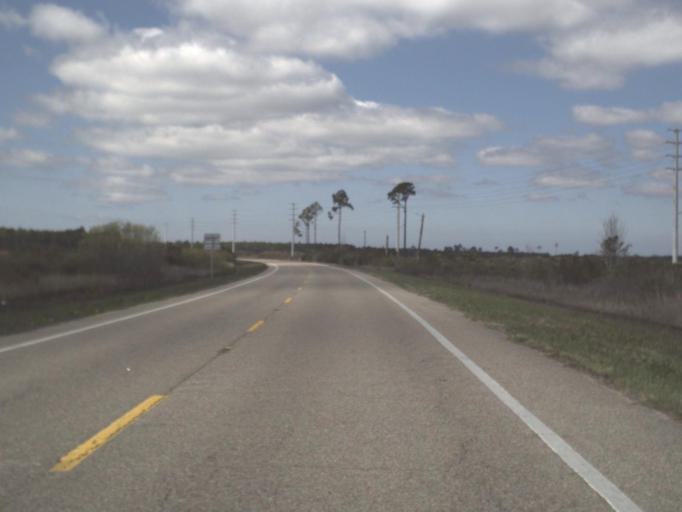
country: US
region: Florida
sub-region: Franklin County
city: Apalachicola
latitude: 29.7257
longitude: -85.0847
